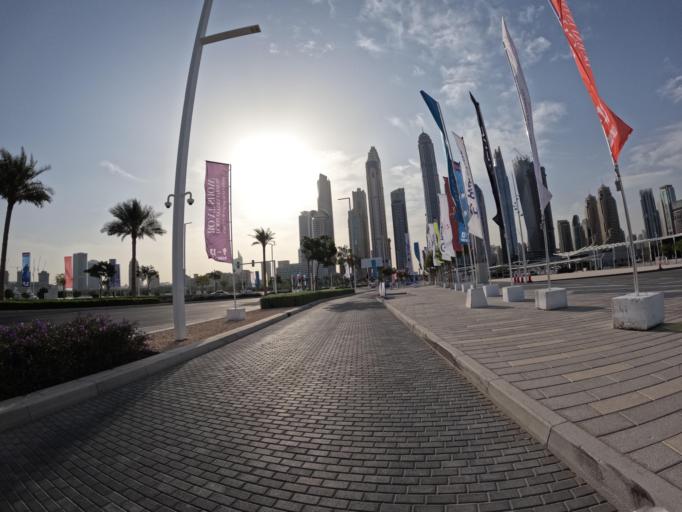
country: AE
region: Dubai
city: Dubai
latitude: 25.0937
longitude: 55.1415
